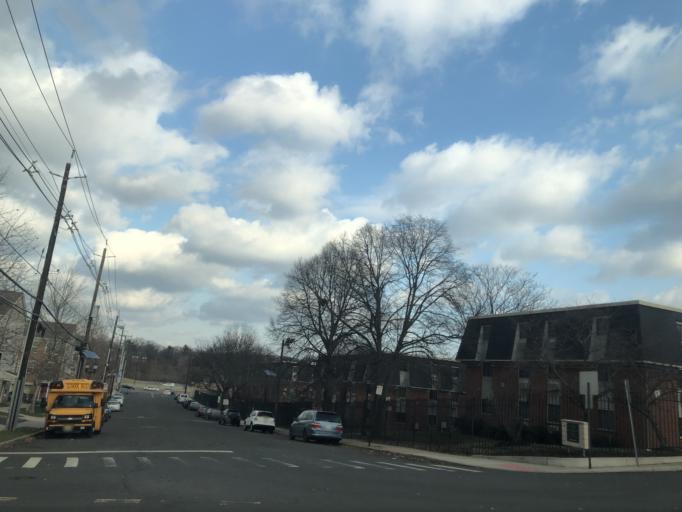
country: US
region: New Jersey
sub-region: Middlesex County
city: New Brunswick
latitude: 40.4906
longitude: -74.4406
